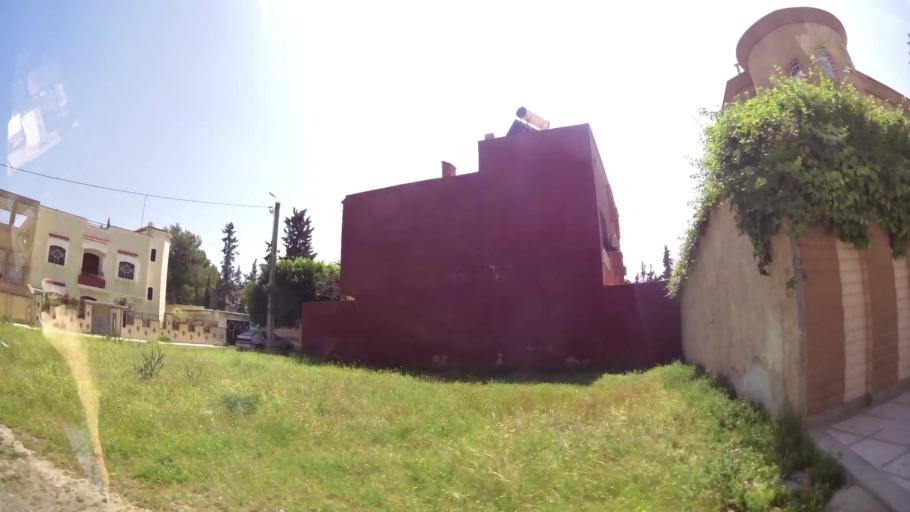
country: MA
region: Oriental
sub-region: Oujda-Angad
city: Oujda
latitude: 34.6852
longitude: -1.8784
